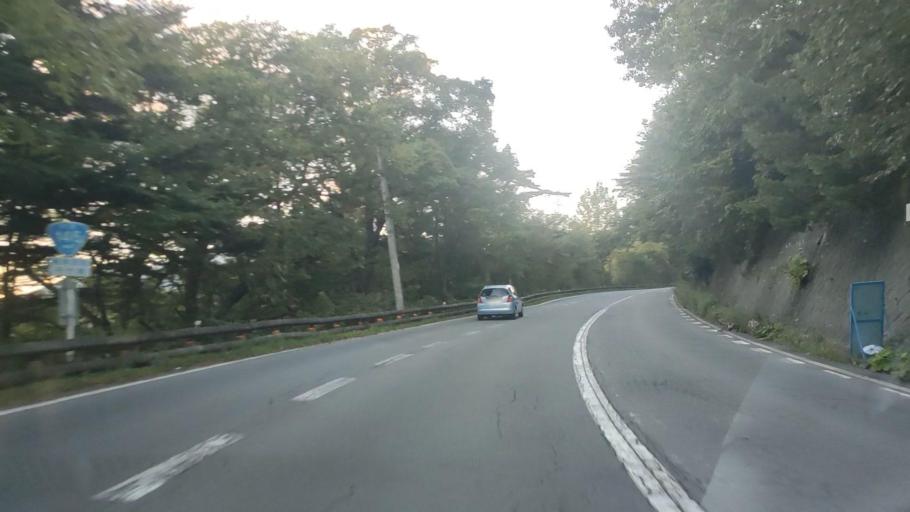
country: JP
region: Nagano
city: Komoro
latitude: 36.3825
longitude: 138.5889
